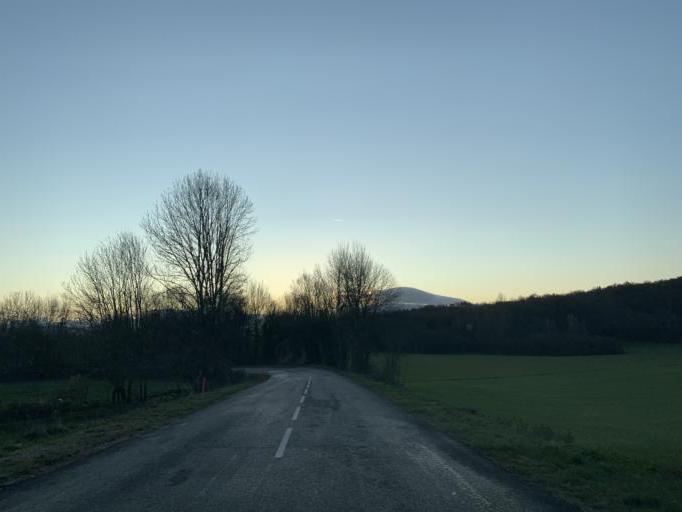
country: FR
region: Rhone-Alpes
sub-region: Departement de l'Ain
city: Belley
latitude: 45.7887
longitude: 5.6466
